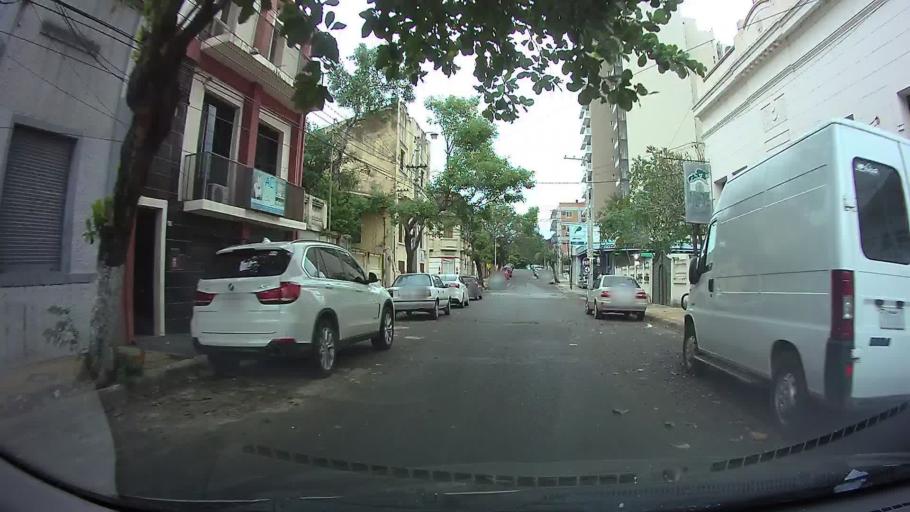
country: PY
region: Asuncion
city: Asuncion
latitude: -25.2906
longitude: -57.6422
